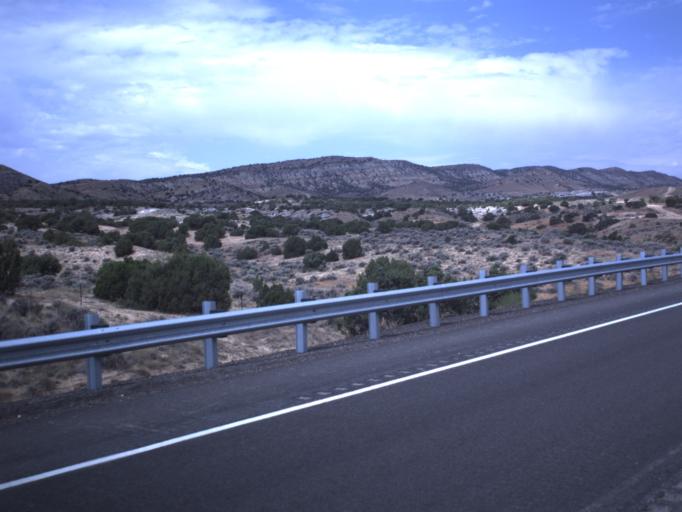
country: US
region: Utah
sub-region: Uintah County
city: Naples
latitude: 40.3551
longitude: -109.4965
